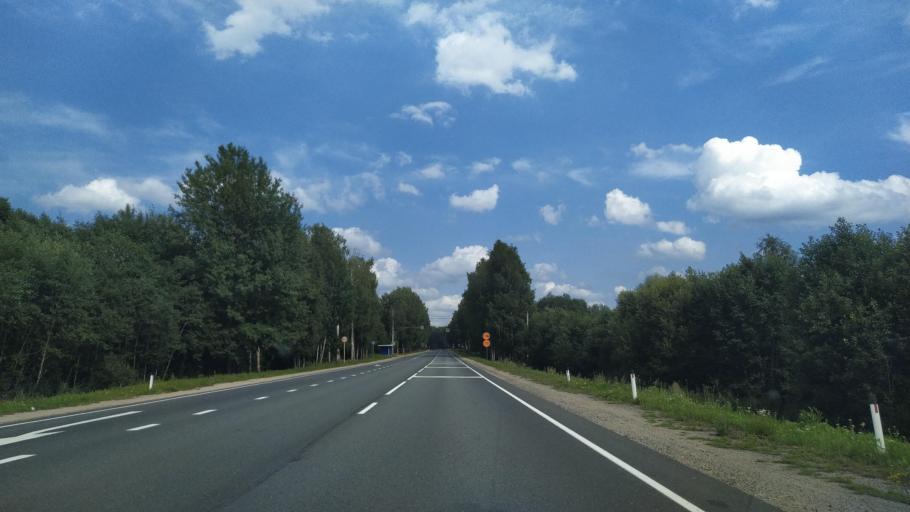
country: RU
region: Pskov
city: Dno
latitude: 57.9831
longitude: 29.7789
